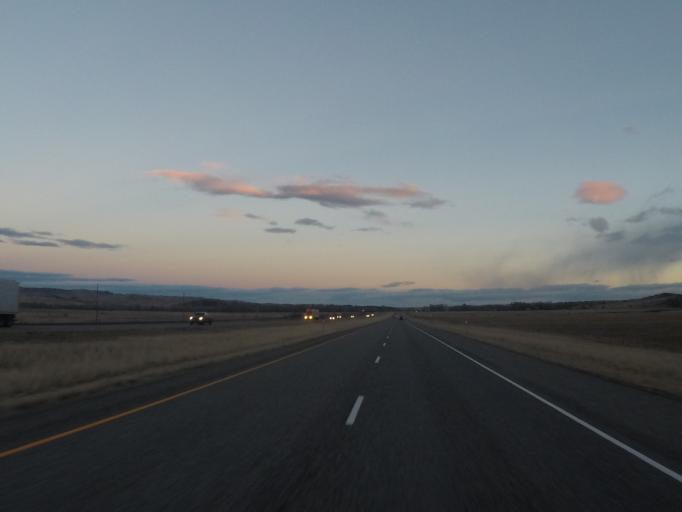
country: US
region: Montana
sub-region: Sweet Grass County
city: Big Timber
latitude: 45.7874
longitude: -109.8210
